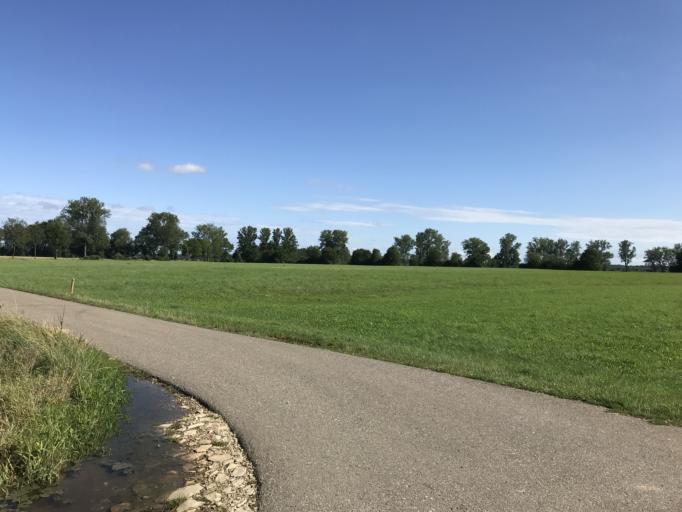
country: DE
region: Baden-Wuerttemberg
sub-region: Tuebingen Region
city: Langenau
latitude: 48.4749
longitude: 10.1210
